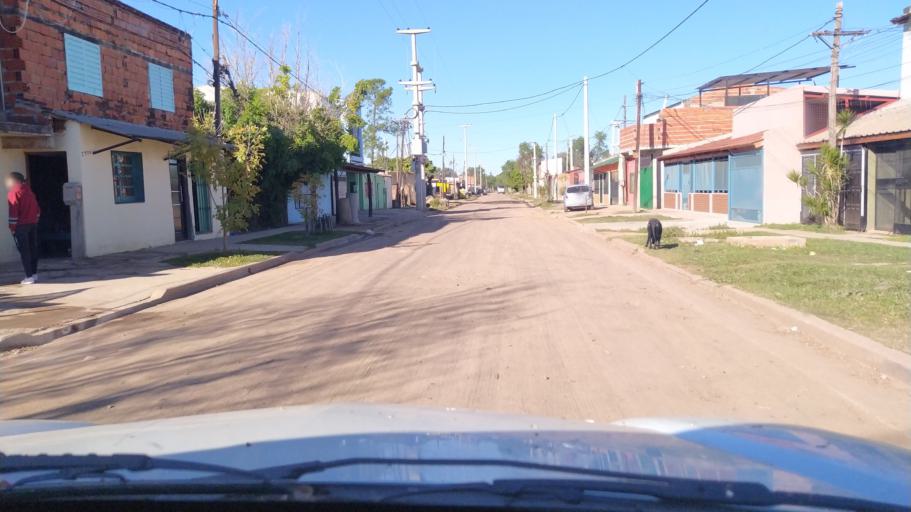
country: AR
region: Corrientes
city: Corrientes
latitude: -27.4938
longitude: -58.8090
